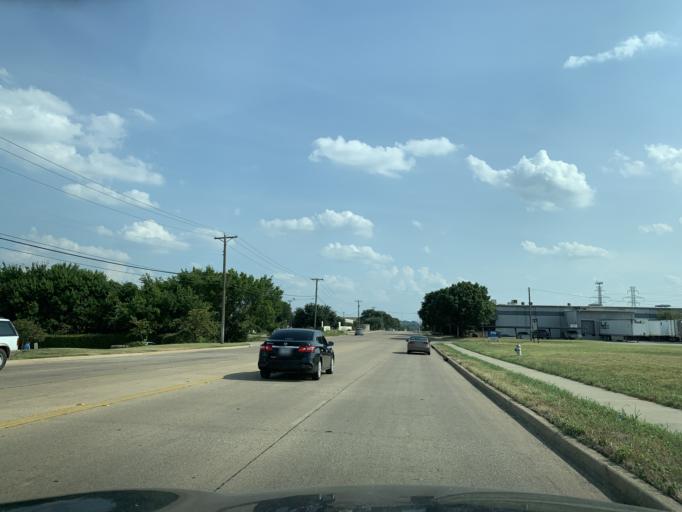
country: US
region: Texas
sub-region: Tarrant County
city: Richland Hills
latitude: 32.7974
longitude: -97.2213
